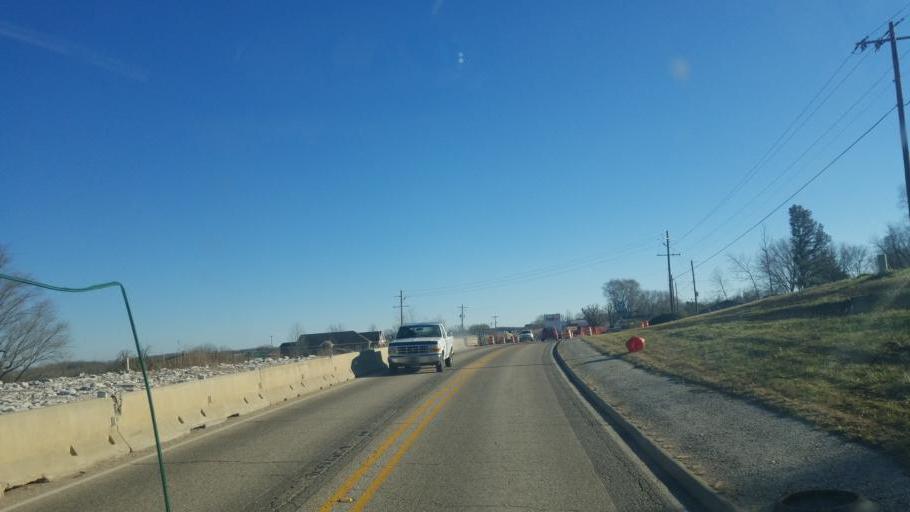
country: US
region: Arkansas
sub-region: Boone County
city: Harrison
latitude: 36.1551
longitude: -92.9914
